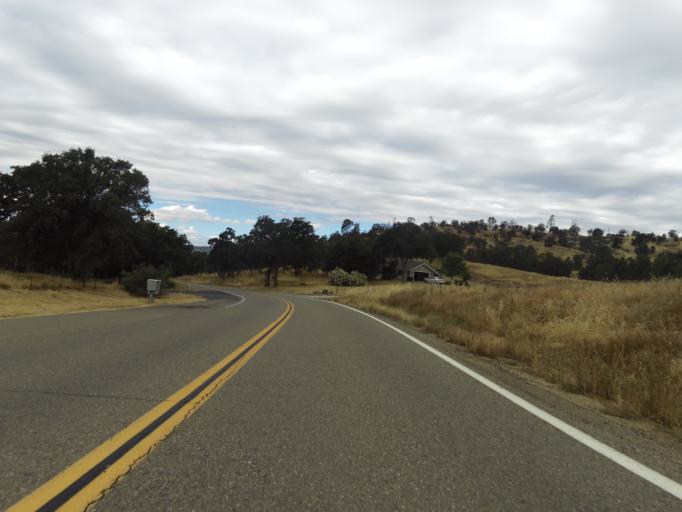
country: US
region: California
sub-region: Madera County
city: Yosemite Lakes
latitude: 37.2313
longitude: -119.7456
